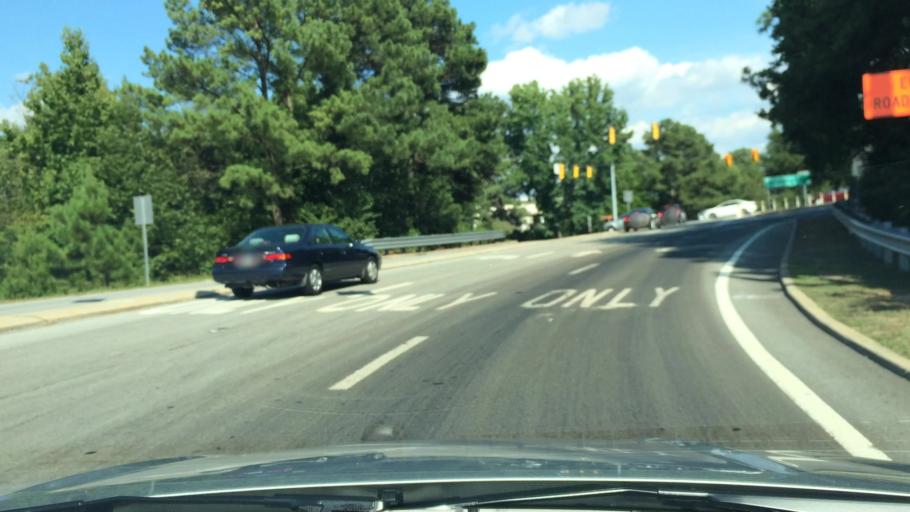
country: US
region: South Carolina
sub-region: Lexington County
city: Seven Oaks
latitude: 34.0794
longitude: -81.1524
